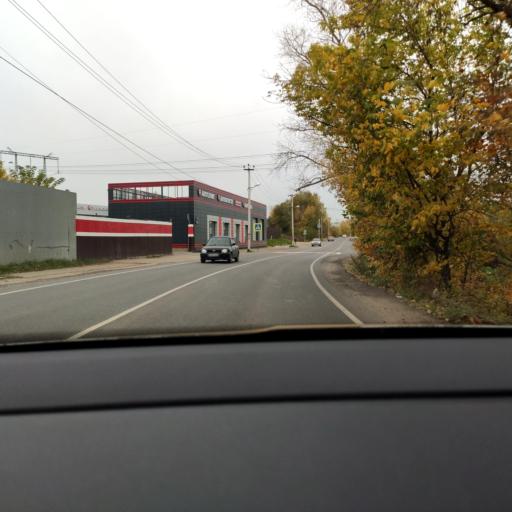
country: RU
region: Moskovskaya
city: Ivanteyevka
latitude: 55.9769
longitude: 37.9339
